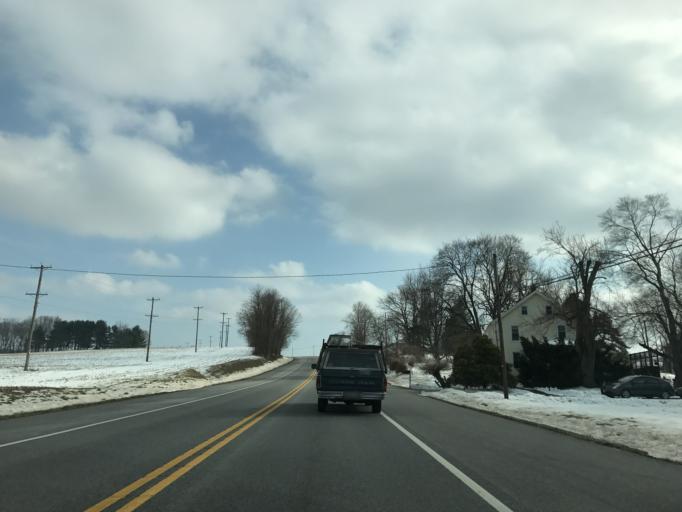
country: US
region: Pennsylvania
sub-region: York County
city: Susquehanna Trails
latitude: 39.6734
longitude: -76.2867
